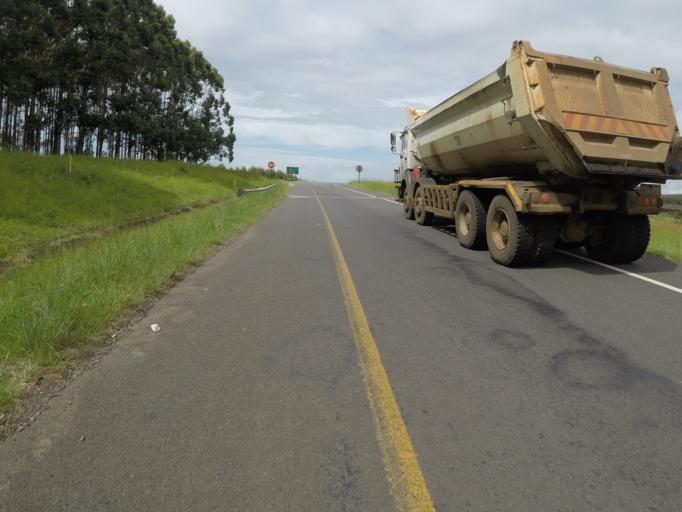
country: ZA
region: KwaZulu-Natal
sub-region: uThungulu District Municipality
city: eSikhawini
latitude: -28.8641
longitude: 31.8869
